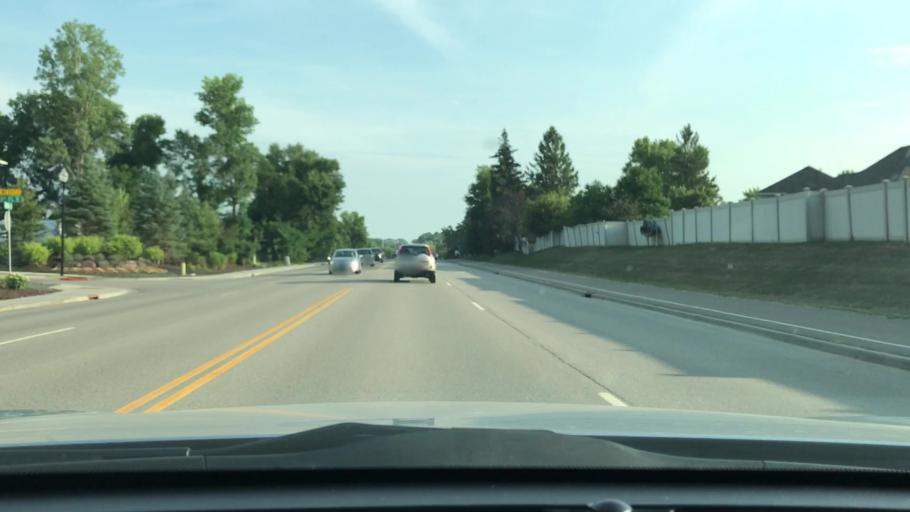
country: US
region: Minnesota
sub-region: Hennepin County
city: Plymouth
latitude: 45.0355
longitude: -93.4818
